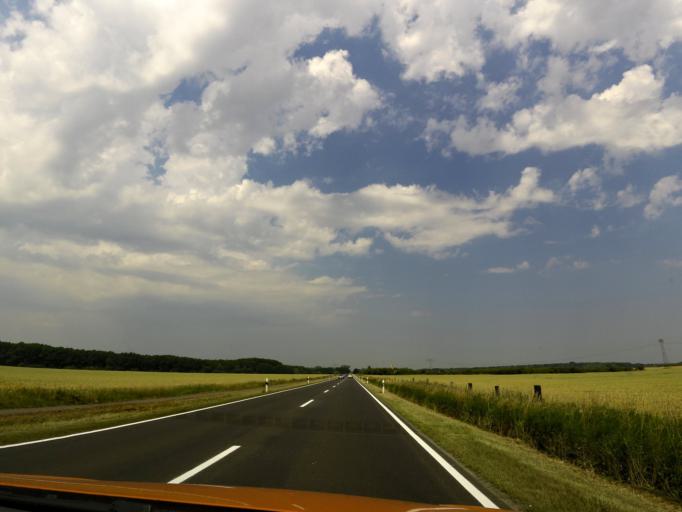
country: DE
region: Brandenburg
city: Wustermark
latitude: 52.4769
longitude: 12.9477
